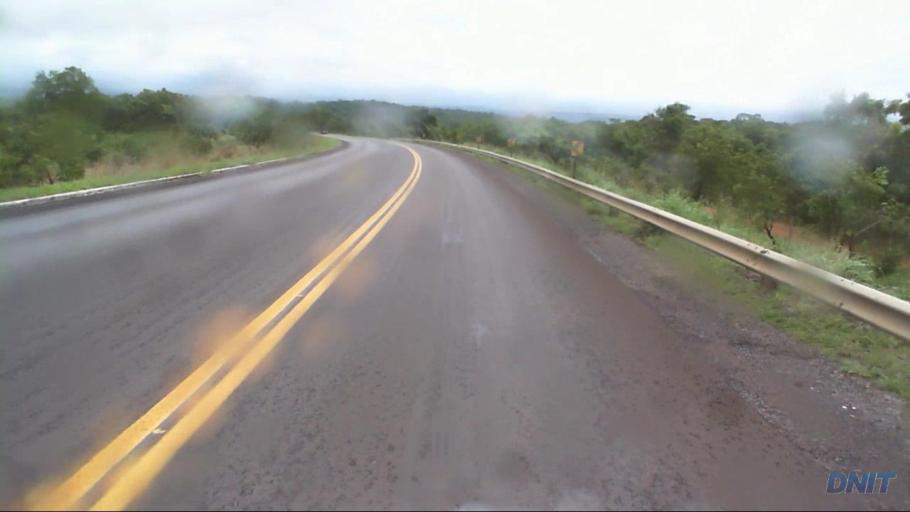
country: BR
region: Goias
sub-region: Padre Bernardo
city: Padre Bernardo
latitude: -15.1942
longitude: -48.4396
